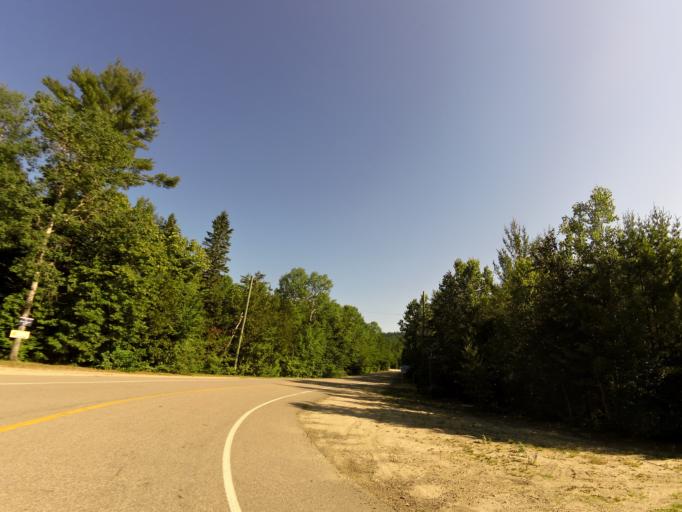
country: CA
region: Ontario
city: Deep River
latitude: 46.1916
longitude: -77.6850
